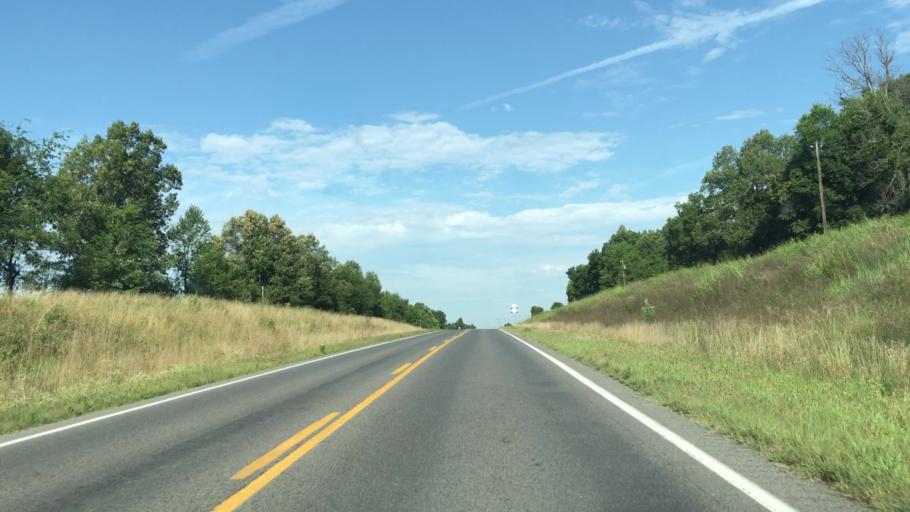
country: US
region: Kentucky
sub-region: Marshall County
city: Calvert City
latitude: 37.0052
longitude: -88.3978
